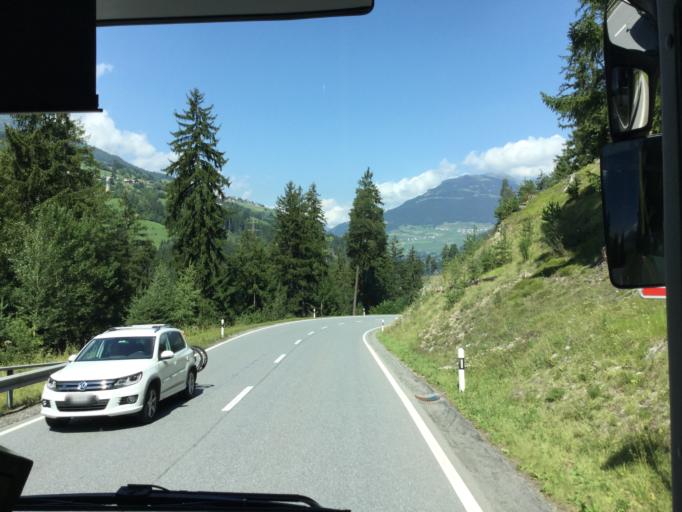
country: CH
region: Grisons
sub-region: Albula District
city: Tiefencastel
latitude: 46.6468
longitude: 9.5818
